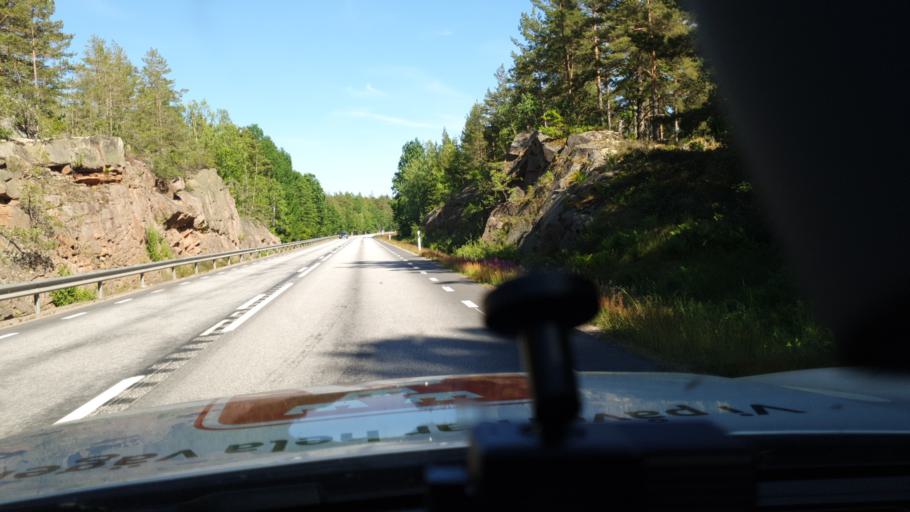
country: SE
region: Kalmar
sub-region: Vasterviks Kommun
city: Ankarsrum
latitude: 57.7147
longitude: 16.1025
